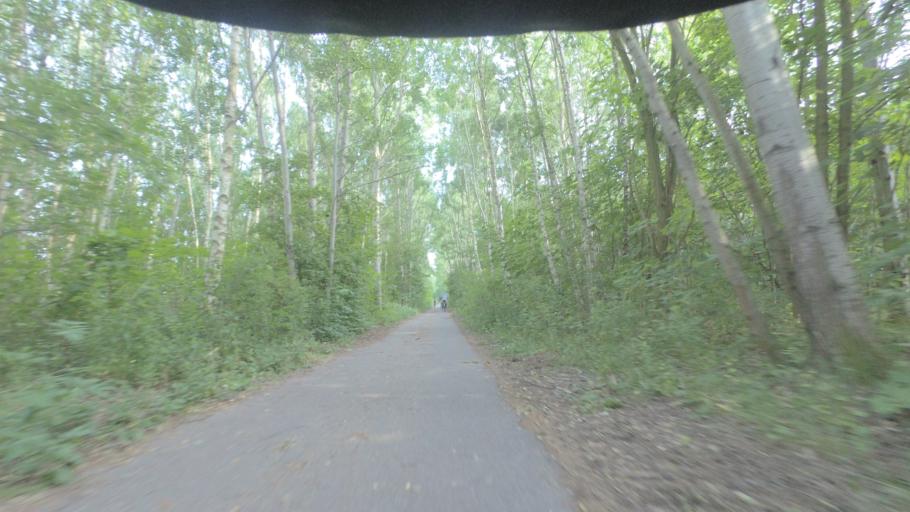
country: DE
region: Berlin
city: Lichtenrade
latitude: 52.3900
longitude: 13.4268
